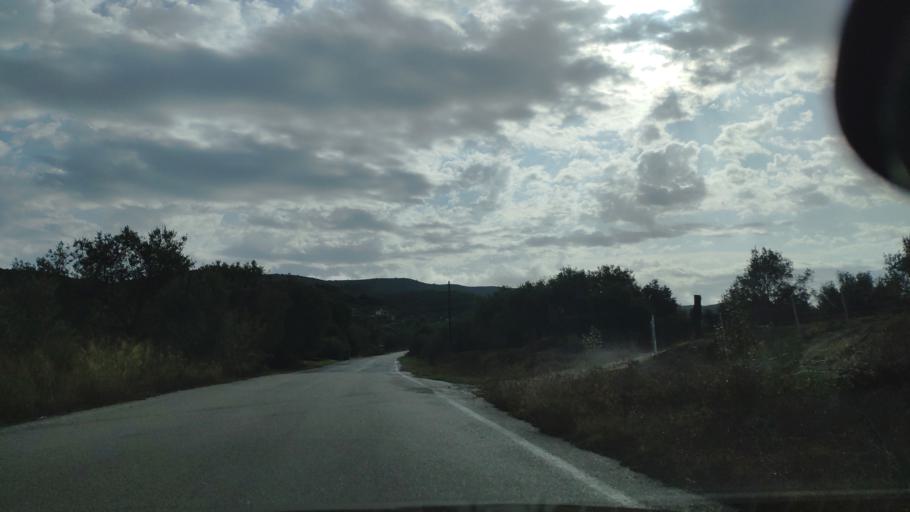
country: GR
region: West Greece
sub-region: Nomos Aitolias kai Akarnanias
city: Sardinia
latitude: 38.8905
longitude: 21.2227
